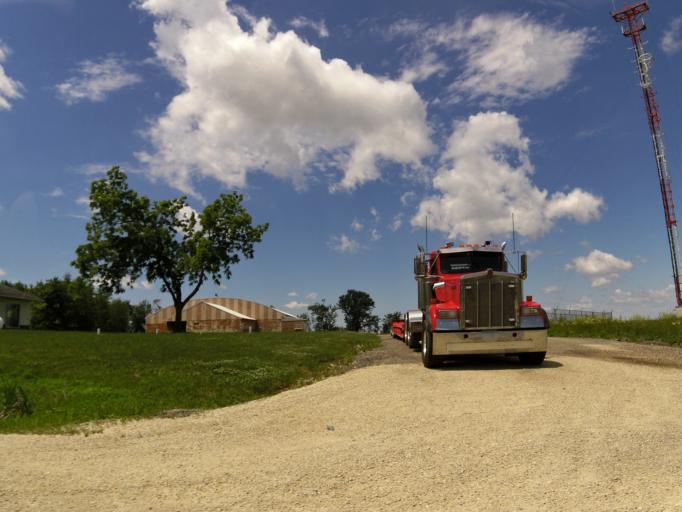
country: US
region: Iowa
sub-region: Fayette County
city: Oelwein
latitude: 42.6914
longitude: -91.9133
